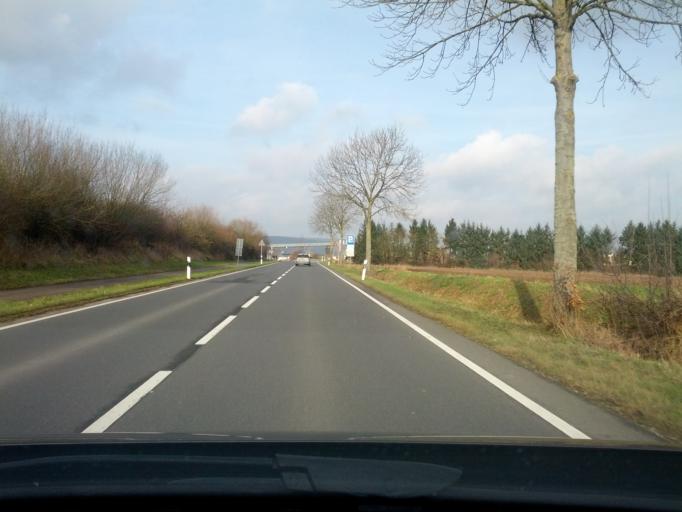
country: DE
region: North Rhine-Westphalia
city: Beverungen
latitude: 51.6471
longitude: 9.3927
